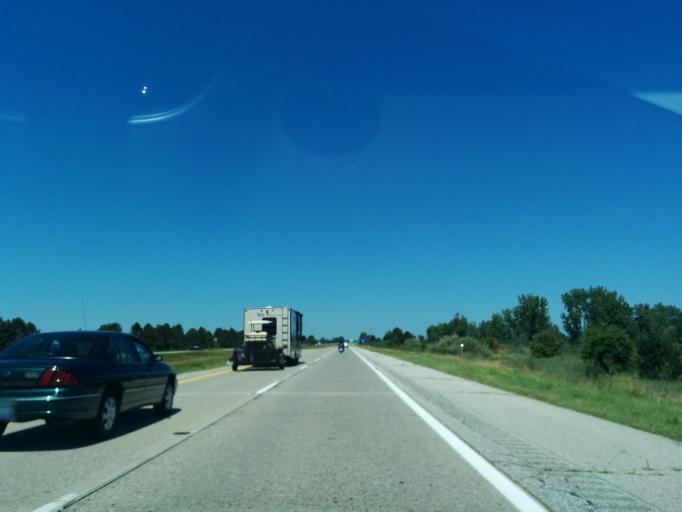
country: US
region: Michigan
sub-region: Bay County
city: Auburn
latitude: 43.6565
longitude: -83.9980
